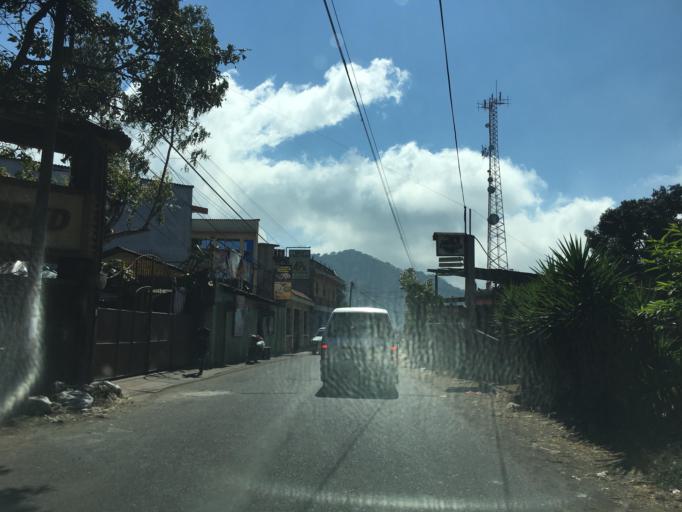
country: GT
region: Solola
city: San Lucas Toliman
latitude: 14.6376
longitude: -91.1467
